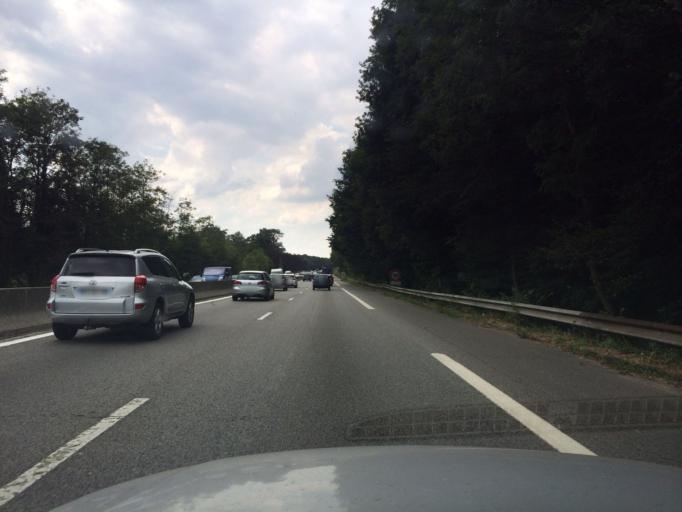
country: FR
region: Ile-de-France
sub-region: Departement des Yvelines
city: Bailly
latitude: 48.8455
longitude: 2.0855
